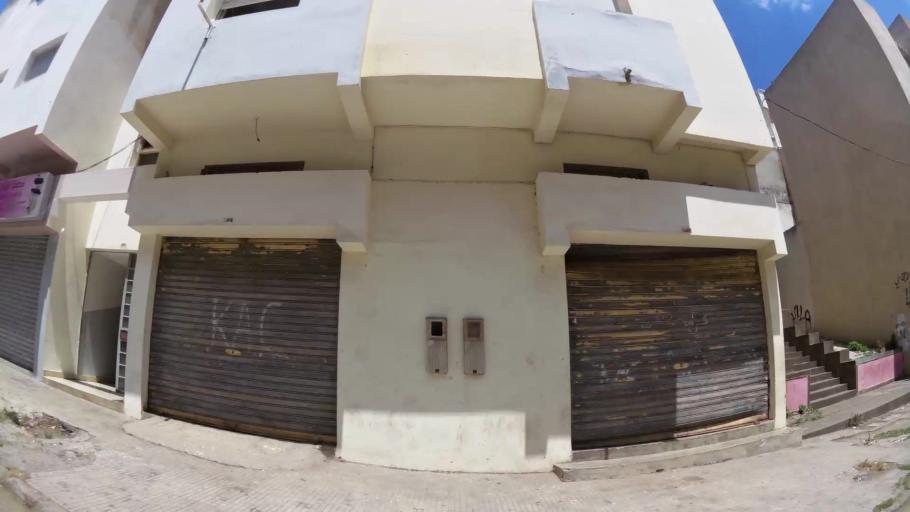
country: MA
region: Gharb-Chrarda-Beni Hssen
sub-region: Kenitra Province
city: Kenitra
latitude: 34.2687
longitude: -6.6052
